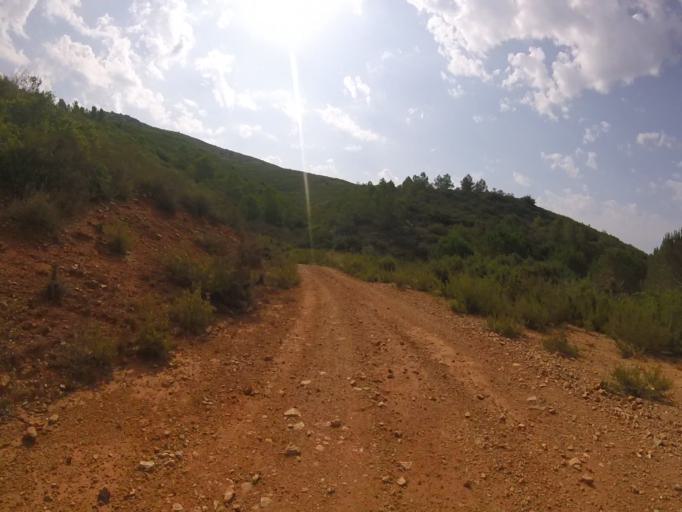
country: ES
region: Valencia
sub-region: Provincia de Castello
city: Alcala de Xivert
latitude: 40.3499
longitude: 0.1987
